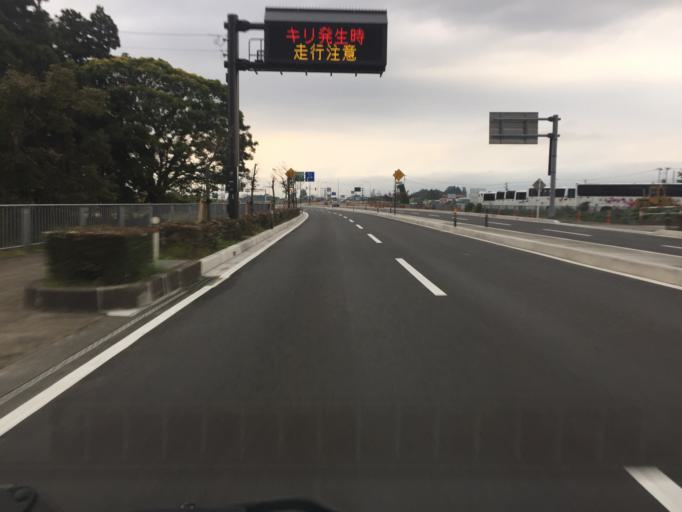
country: JP
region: Fukushima
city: Kitakata
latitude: 37.5329
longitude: 139.9154
